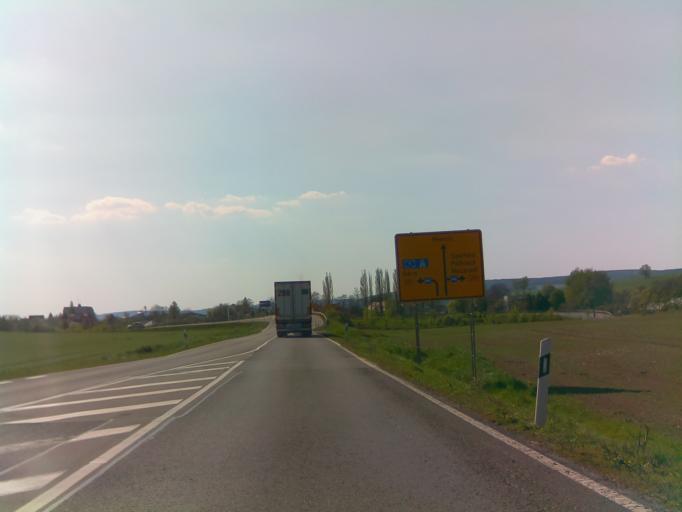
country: DE
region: Thuringia
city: Miesitz
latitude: 50.7381
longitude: 11.8441
